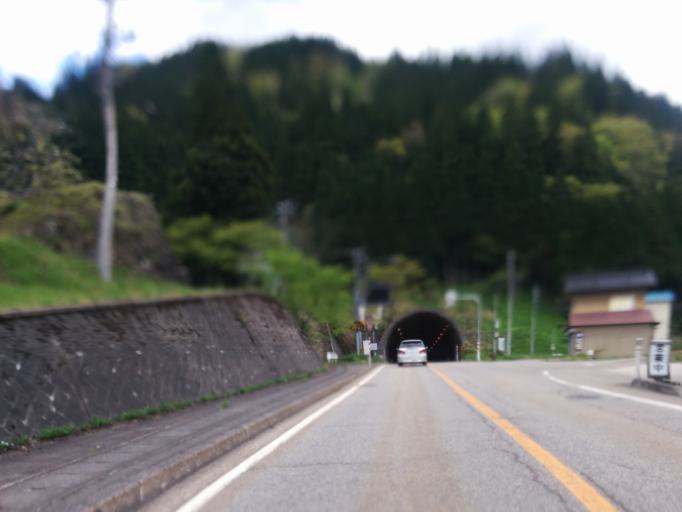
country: JP
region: Toyama
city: Fukumitsu
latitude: 36.4123
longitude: 136.9320
